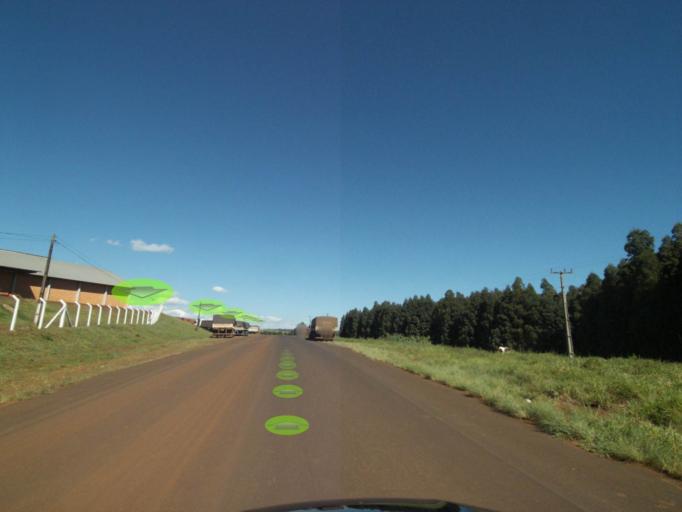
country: BR
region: Parana
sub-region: Coronel Vivida
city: Coronel Vivida
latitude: -26.1486
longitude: -52.3668
